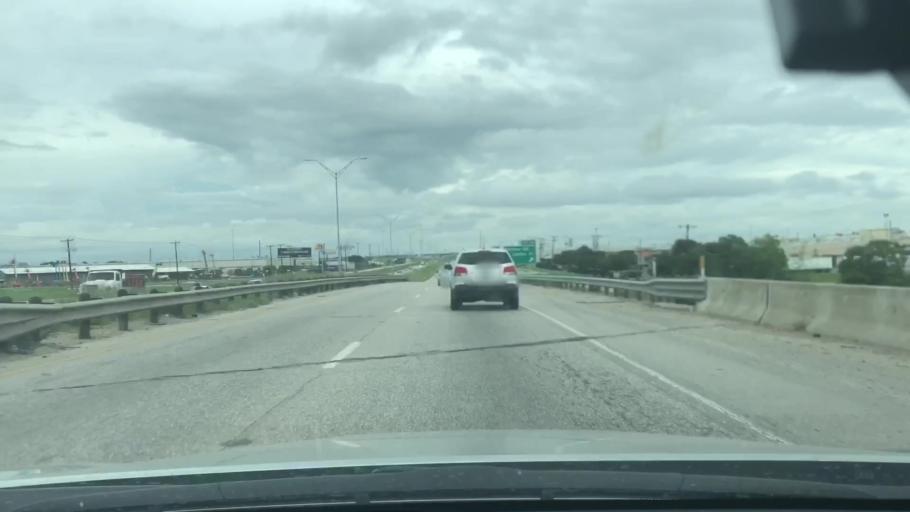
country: US
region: Texas
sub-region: Bexar County
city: Kirby
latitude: 29.4607
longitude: -98.4040
